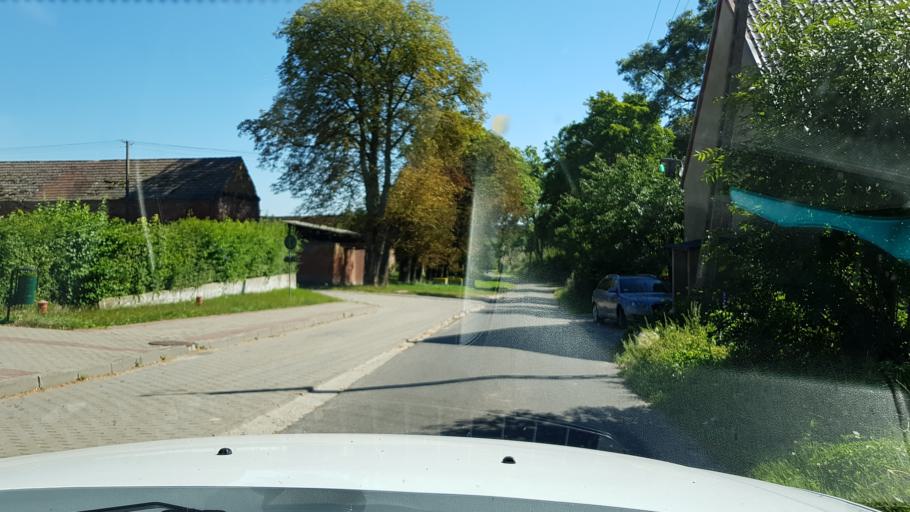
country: PL
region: West Pomeranian Voivodeship
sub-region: Powiat slawienski
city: Darlowo
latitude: 54.4573
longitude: 16.4884
